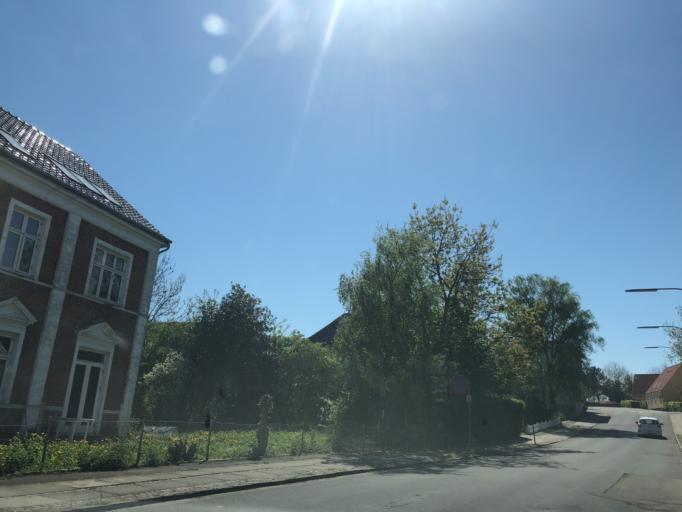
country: DK
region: Zealand
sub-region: Slagelse Kommune
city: Korsor
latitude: 55.3273
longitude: 11.1425
